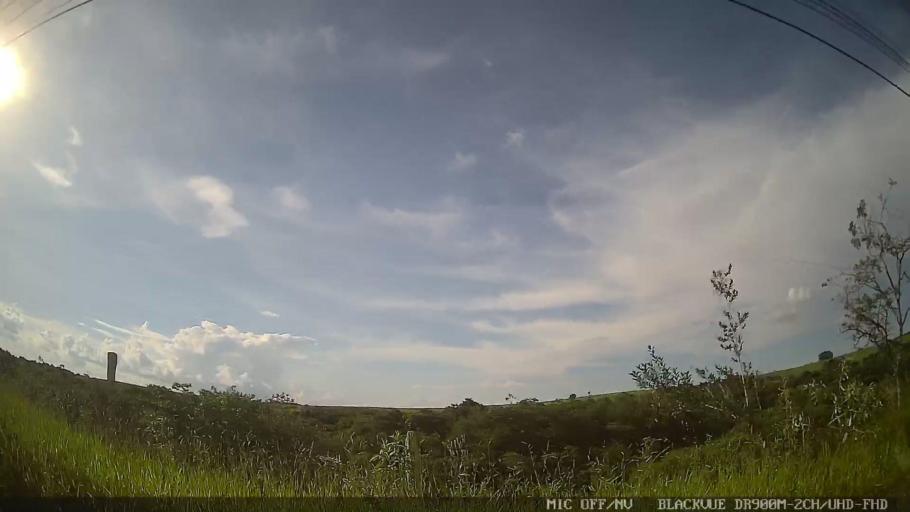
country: BR
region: Sao Paulo
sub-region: Tiete
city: Tiete
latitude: -23.0852
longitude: -47.6897
